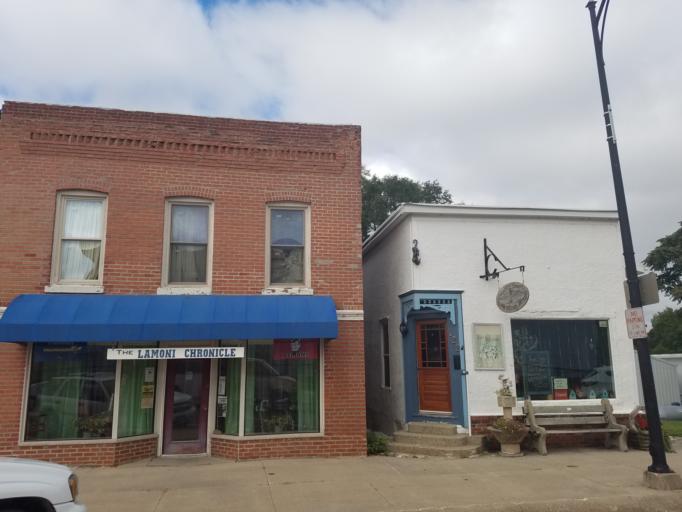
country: US
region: Iowa
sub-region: Decatur County
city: Lamoni
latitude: 40.6236
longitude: -93.9341
